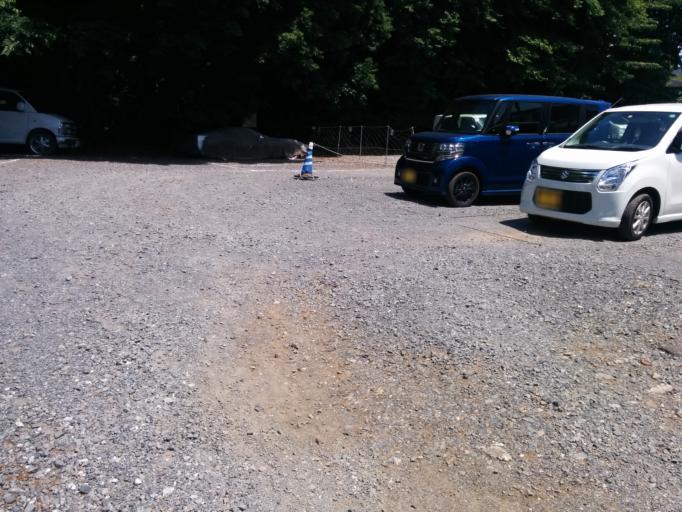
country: JP
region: Tokyo
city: Higashimurayama-shi
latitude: 35.7661
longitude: 139.4577
